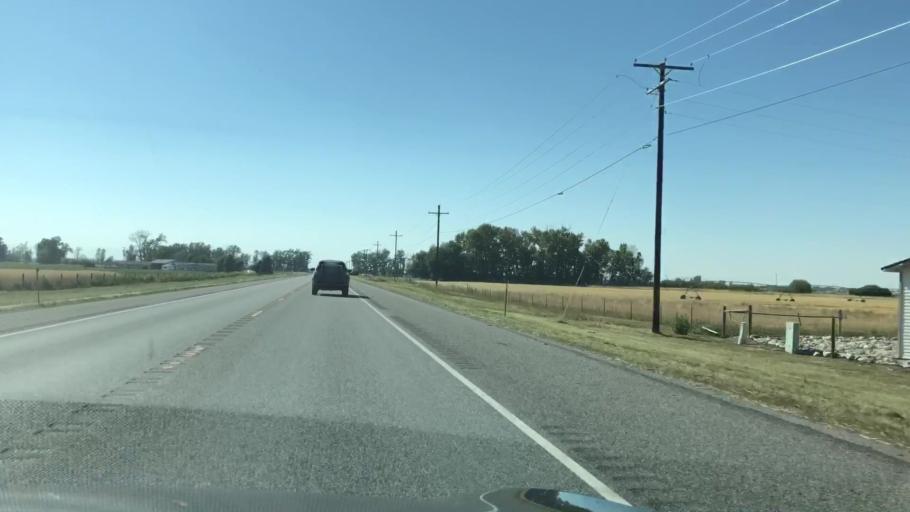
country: US
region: Montana
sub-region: Gallatin County
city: Belgrade
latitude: 45.7292
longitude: -111.1599
